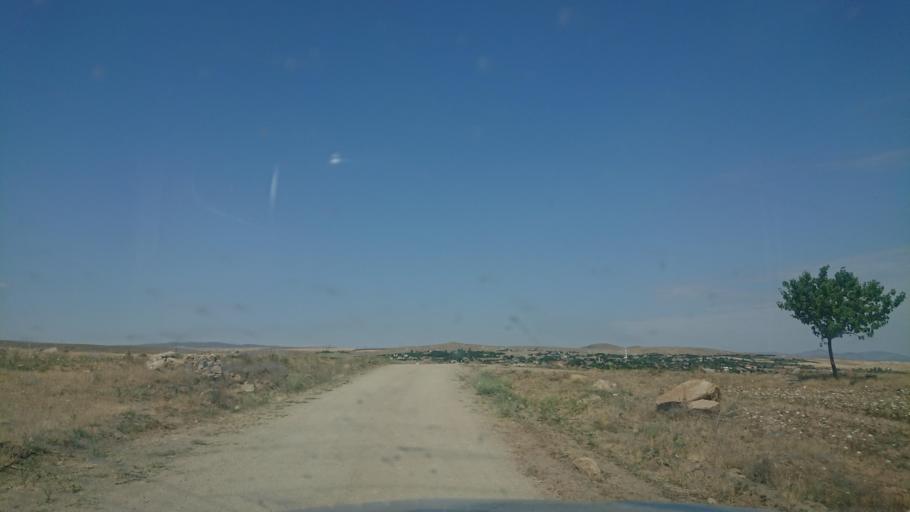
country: TR
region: Aksaray
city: Sariyahsi
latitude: 38.9571
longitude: 33.9056
